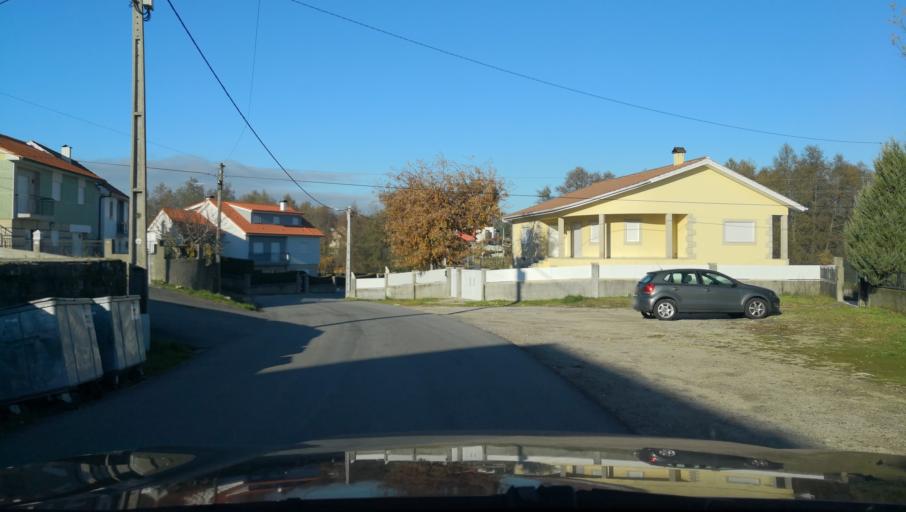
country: PT
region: Vila Real
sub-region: Vila Real
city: Vila Real
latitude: 41.3399
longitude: -7.6634
